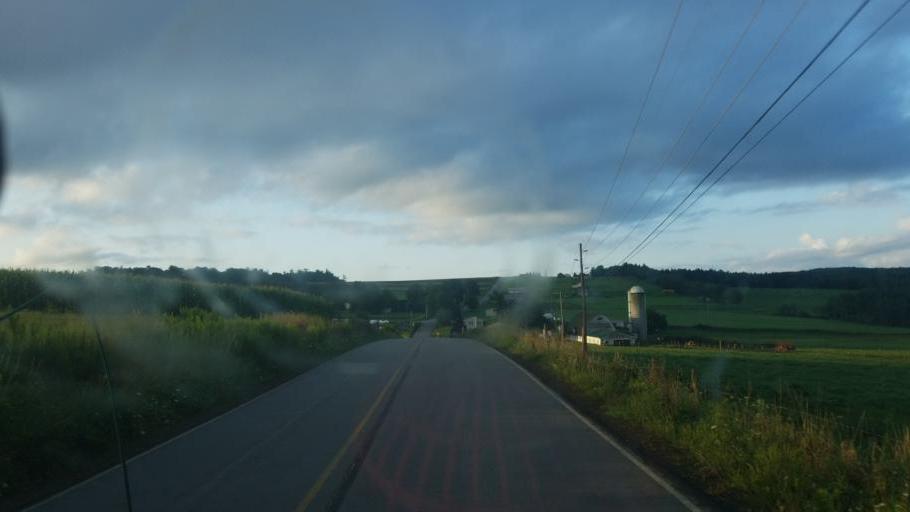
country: US
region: Pennsylvania
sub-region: Potter County
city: Galeton
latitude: 41.8900
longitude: -77.7617
